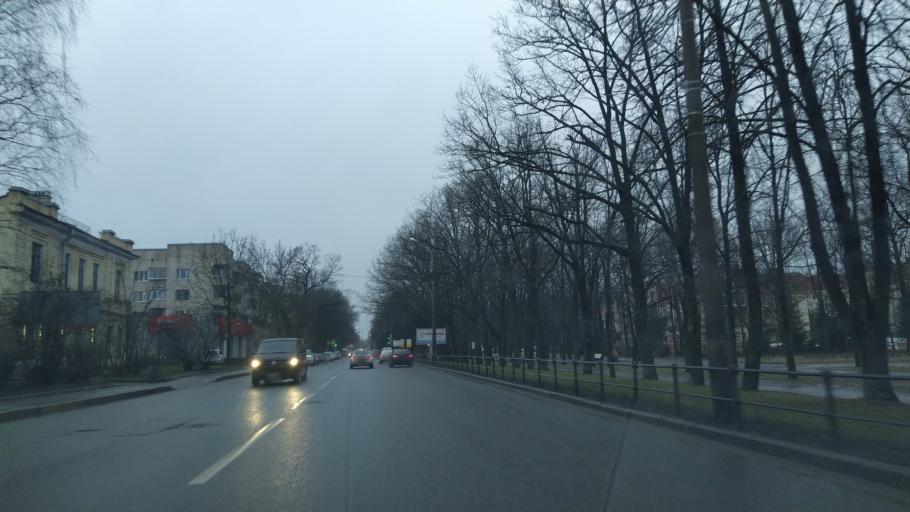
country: RU
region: St.-Petersburg
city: Pushkin
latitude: 59.7246
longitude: 30.4081
